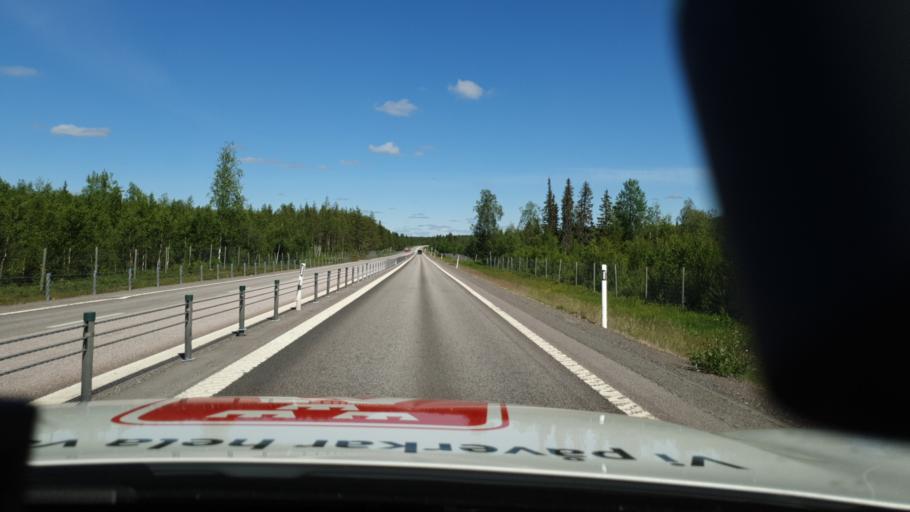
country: SE
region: Norrbotten
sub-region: Lulea Kommun
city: Ranea
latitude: 65.8045
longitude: 22.1939
